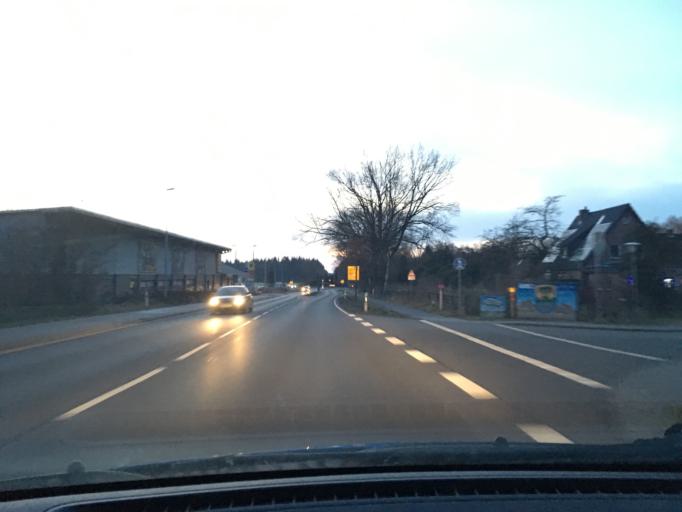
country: DE
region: Lower Saxony
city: Barendorf
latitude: 53.2296
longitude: 10.5178
